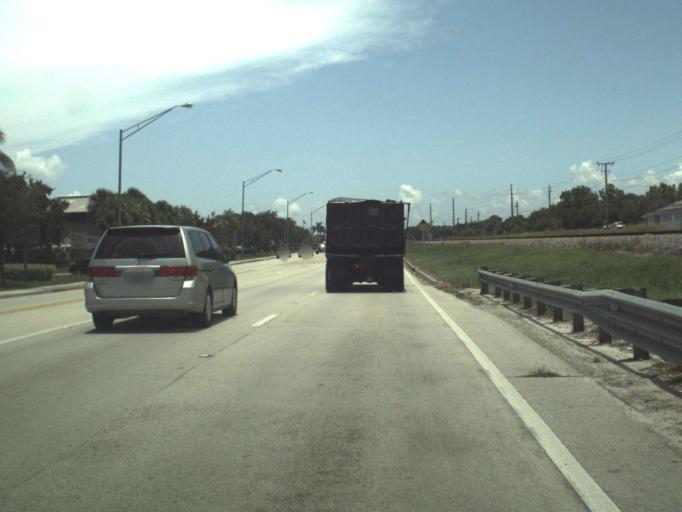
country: US
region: Florida
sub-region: Indian River County
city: Vero Beach
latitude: 27.6492
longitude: -80.4005
